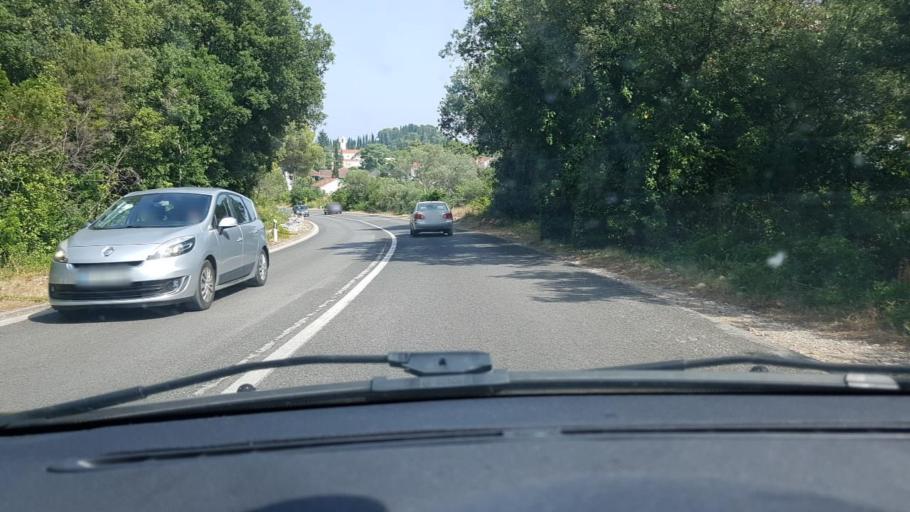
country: HR
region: Dubrovacko-Neretvanska
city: Korcula
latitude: 42.9488
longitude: 17.1323
